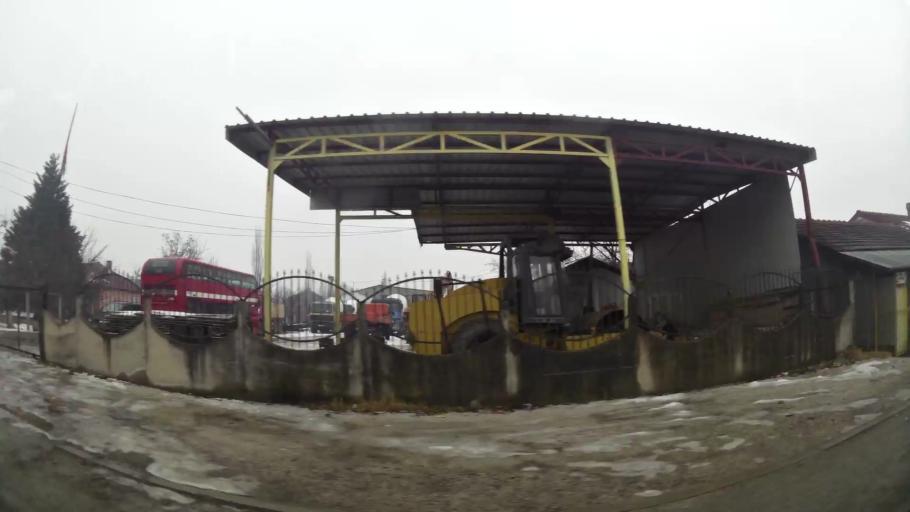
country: MK
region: Petrovec
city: Petrovec
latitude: 41.9283
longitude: 21.6278
